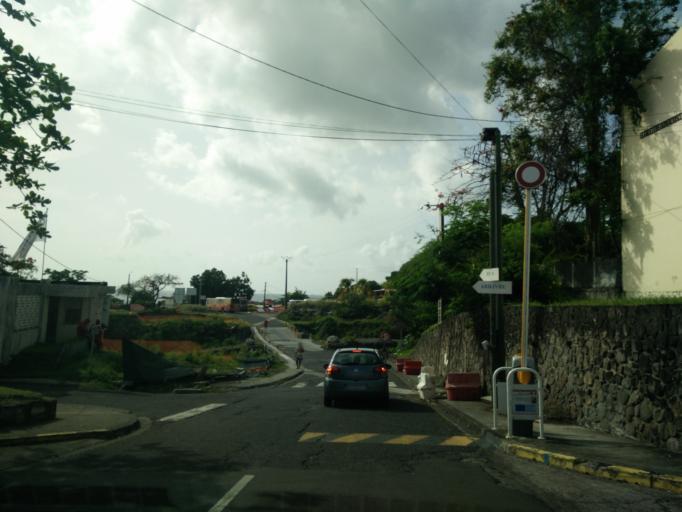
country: MQ
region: Martinique
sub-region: Martinique
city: Saint-Pierre
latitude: 14.8026
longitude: -61.2250
